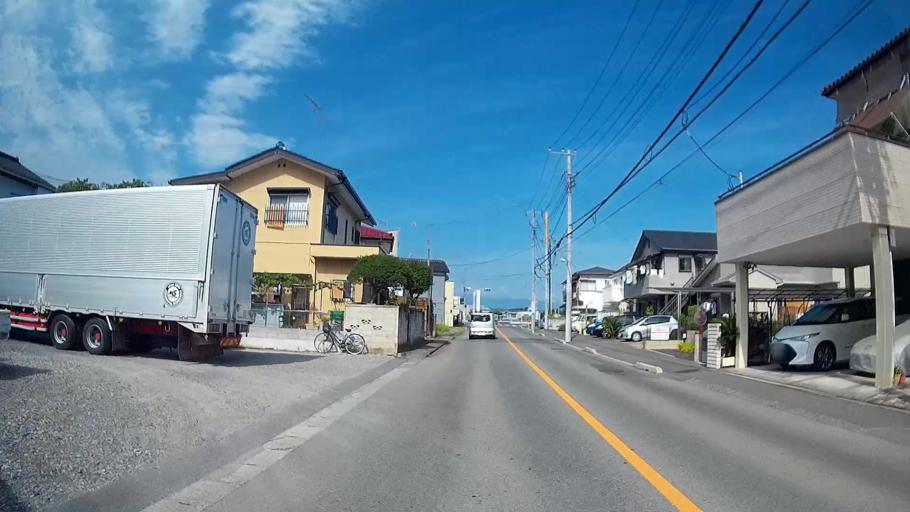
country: JP
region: Saitama
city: Hanno
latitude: 35.8404
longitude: 139.3569
